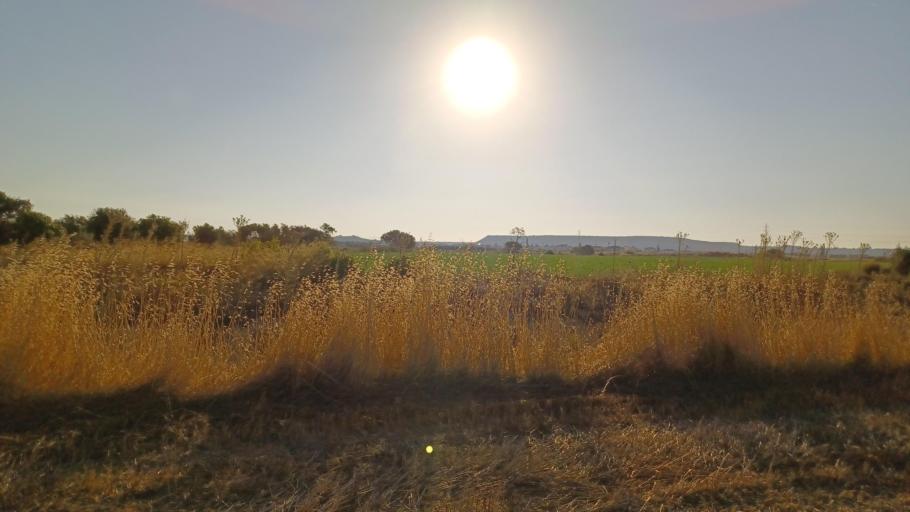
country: CY
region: Larnaka
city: Voroklini
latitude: 34.9902
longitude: 33.6725
